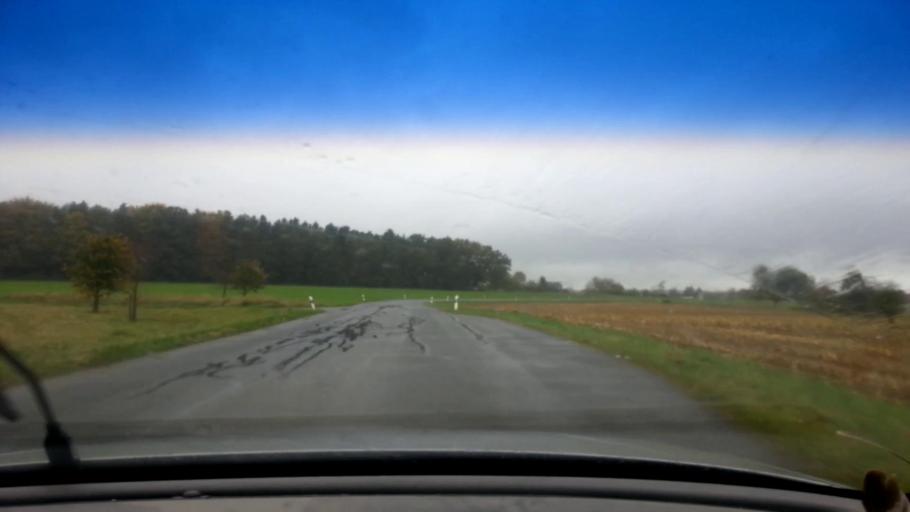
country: DE
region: Bavaria
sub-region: Upper Franconia
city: Stadelhofen
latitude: 50.0136
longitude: 11.1789
